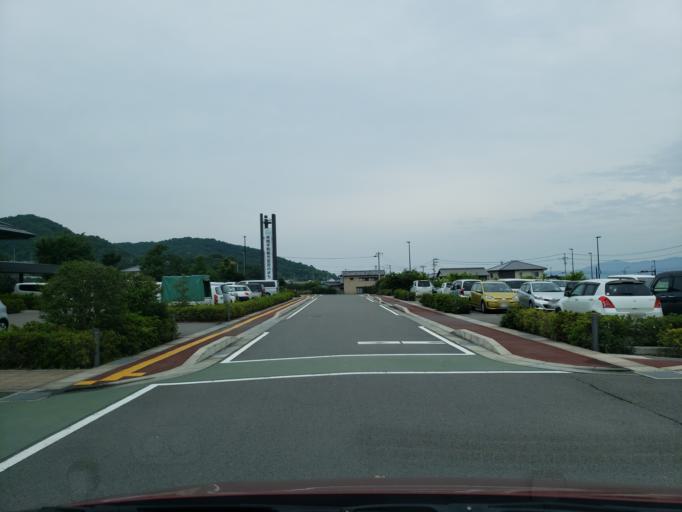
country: JP
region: Tokushima
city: Kamojimacho-jogejima
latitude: 34.1015
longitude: 134.2975
